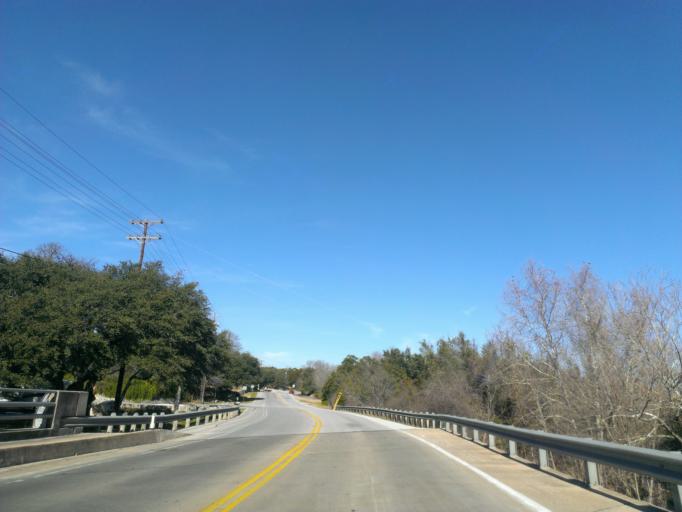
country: US
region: Texas
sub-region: Travis County
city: Lakeway
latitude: 30.3624
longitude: -97.9789
